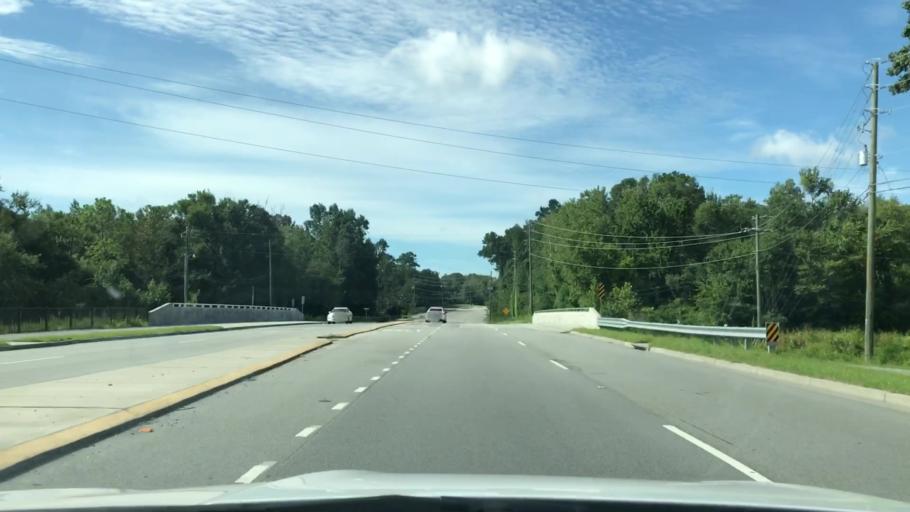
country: US
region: South Carolina
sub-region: Dorchester County
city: Centerville
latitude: 32.9742
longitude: -80.1982
